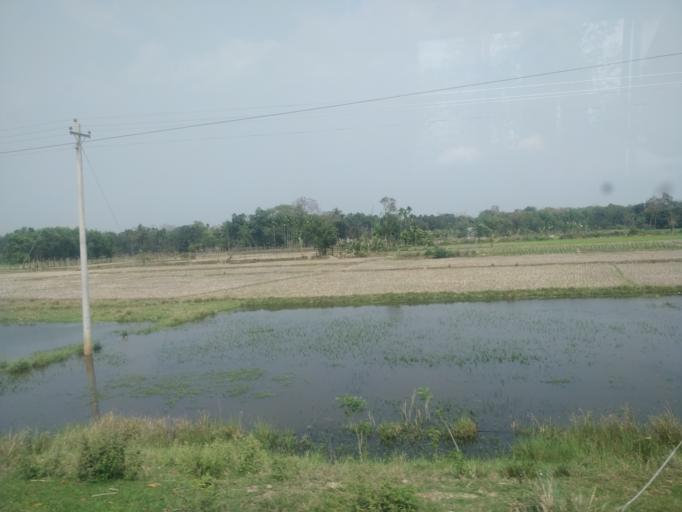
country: BD
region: Sylhet
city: Habiganj
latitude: 24.3218
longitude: 91.4343
